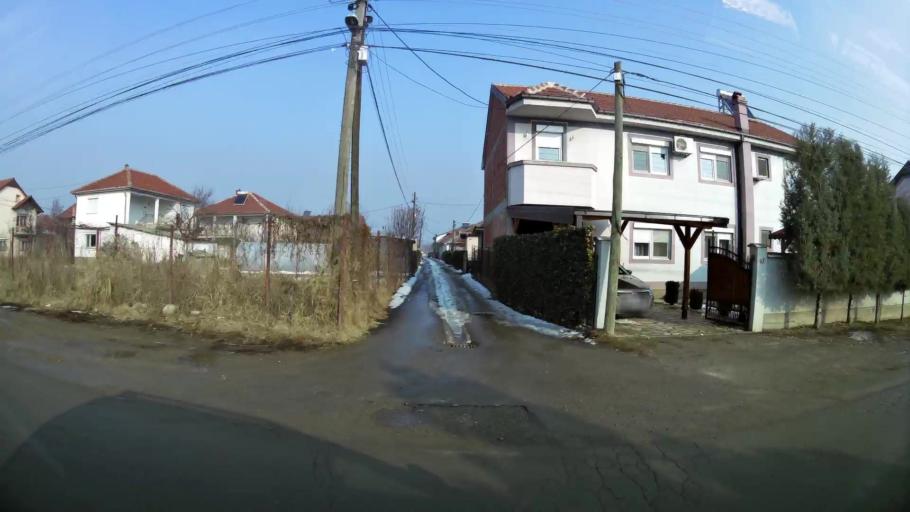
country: MK
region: Ilinden
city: Marino
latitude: 41.9816
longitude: 21.5923
